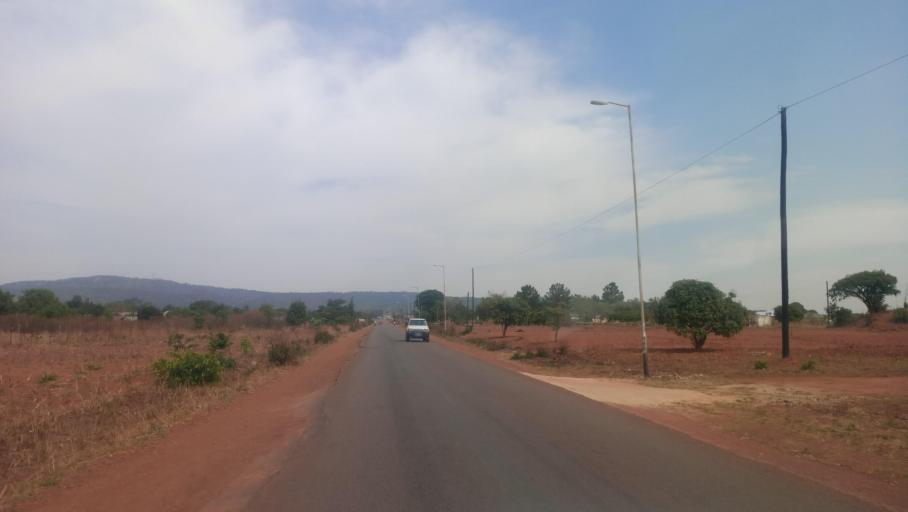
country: ZM
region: Northern
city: Mpika
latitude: -11.8385
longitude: 31.4335
